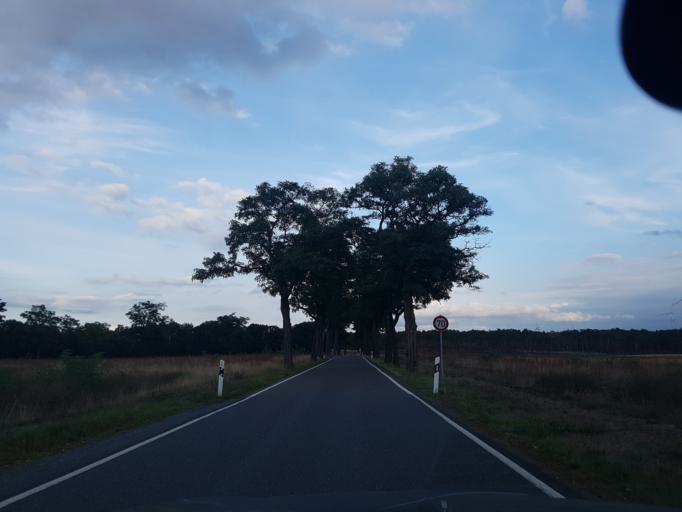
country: DE
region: Brandenburg
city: Schlieben
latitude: 51.6807
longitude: 13.3535
